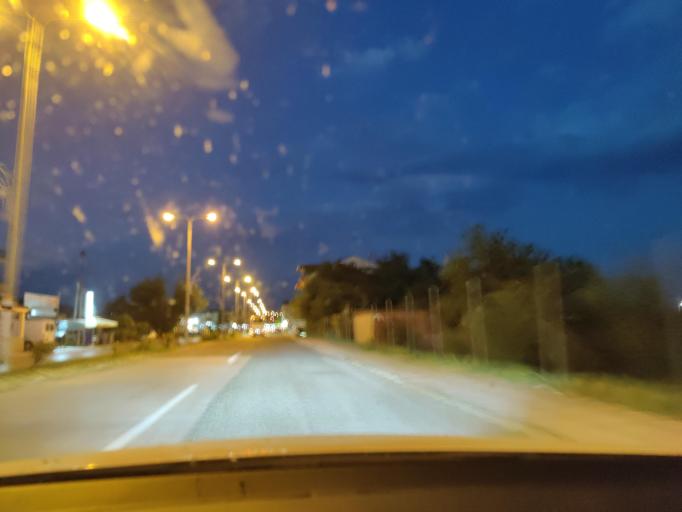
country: GR
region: Central Macedonia
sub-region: Nomos Serron
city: Lefkonas
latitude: 41.0998
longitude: 23.4916
